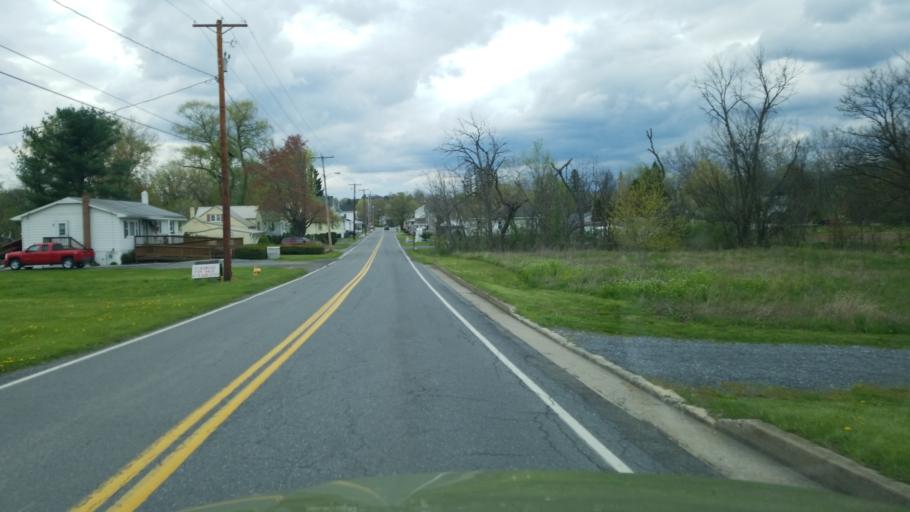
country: US
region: Pennsylvania
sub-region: Blair County
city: Hollidaysburg
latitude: 40.4210
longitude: -78.3936
